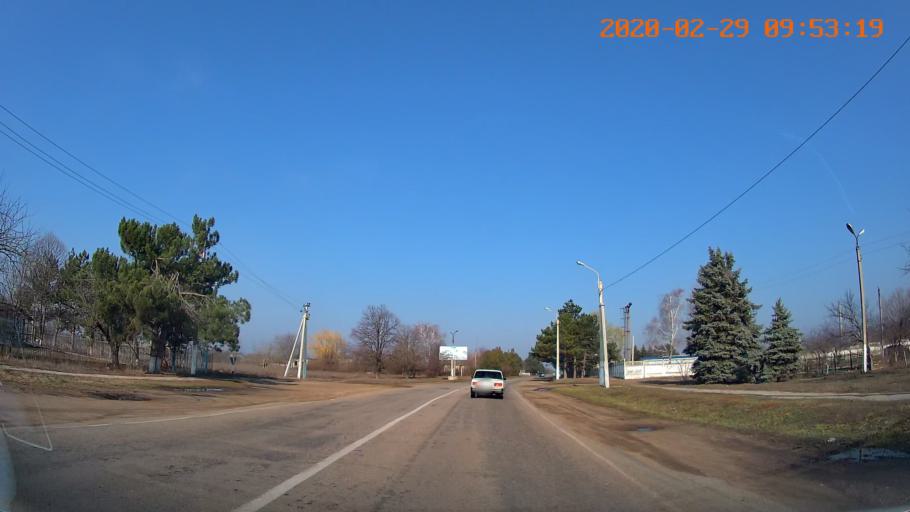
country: MD
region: Telenesti
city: Slobozia
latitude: 46.7212
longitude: 29.7225
